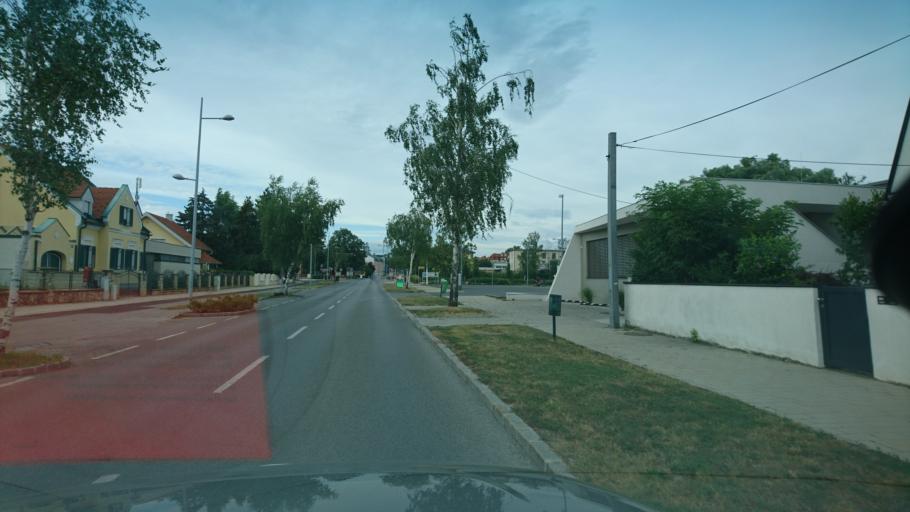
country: AT
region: Burgenland
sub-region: Politischer Bezirk Neusiedl am See
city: Neusiedl am See
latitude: 47.9411
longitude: 16.8459
